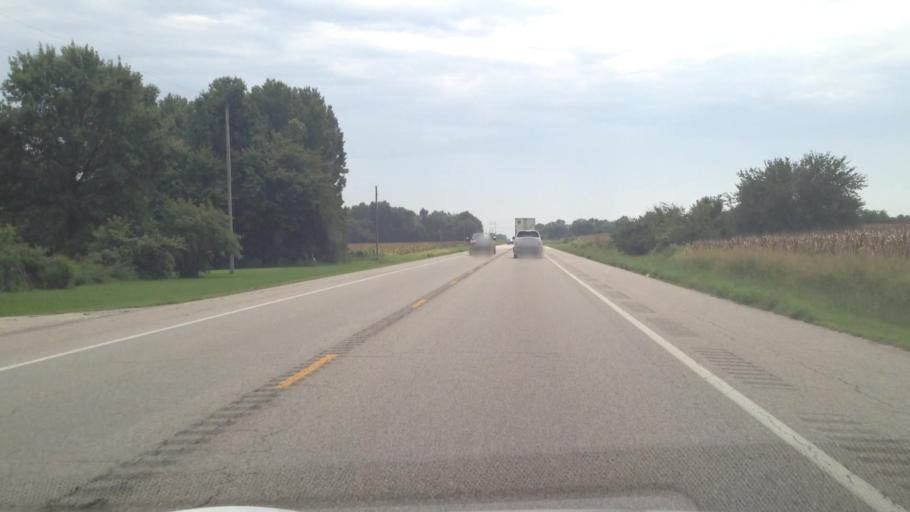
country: US
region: Kansas
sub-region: Crawford County
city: Pittsburg
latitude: 37.3020
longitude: -94.7055
